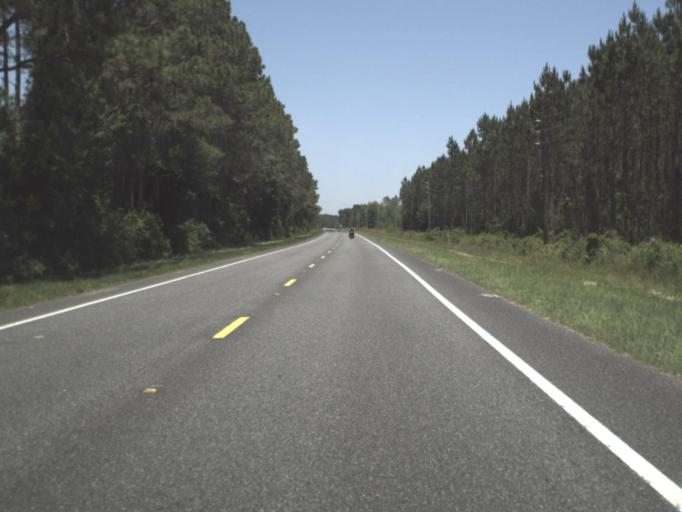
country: US
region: Florida
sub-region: Union County
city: Lake Butler
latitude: 30.2089
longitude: -82.3989
